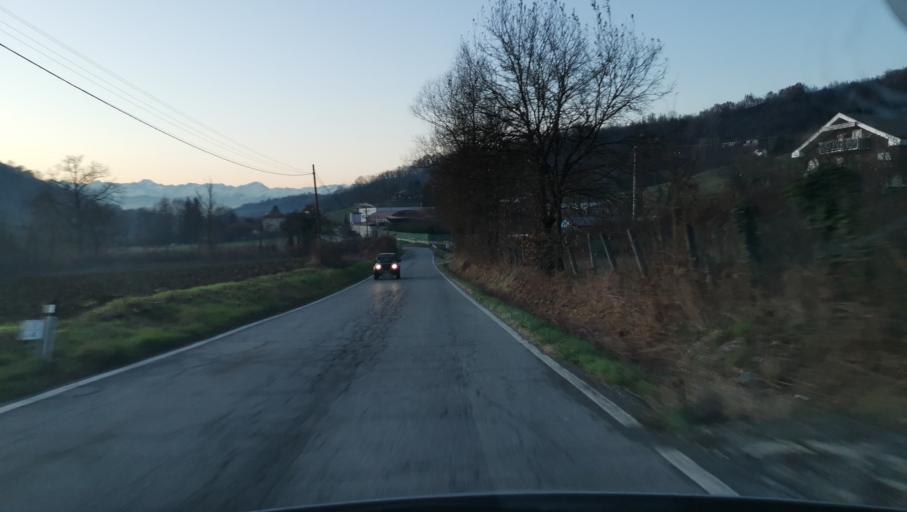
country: IT
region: Piedmont
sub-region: Provincia di Torino
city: Rivalba
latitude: 45.1175
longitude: 7.8679
